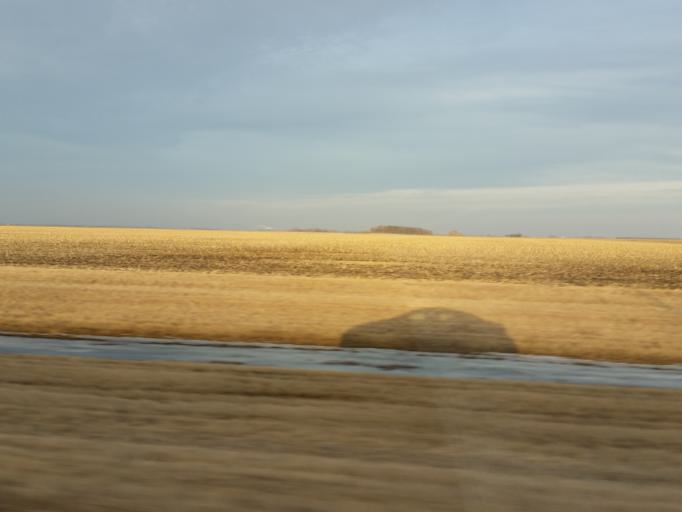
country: US
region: North Dakota
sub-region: Traill County
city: Mayville
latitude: 47.3908
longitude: -97.3263
